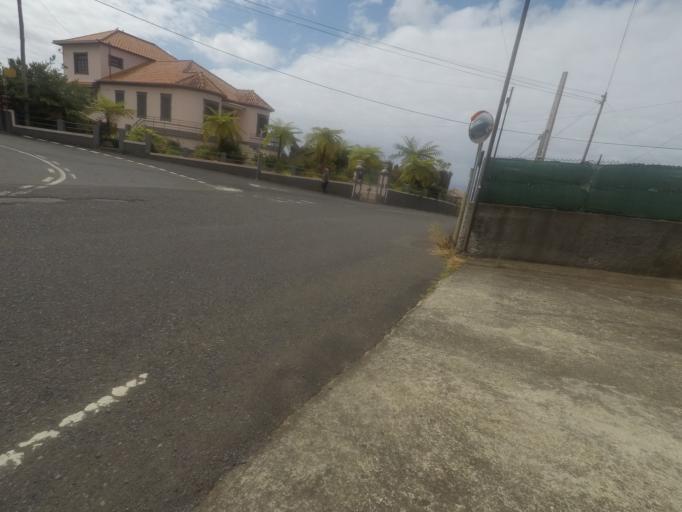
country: PT
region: Madeira
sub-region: Santana
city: Santana
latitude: 32.8120
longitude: -16.8863
